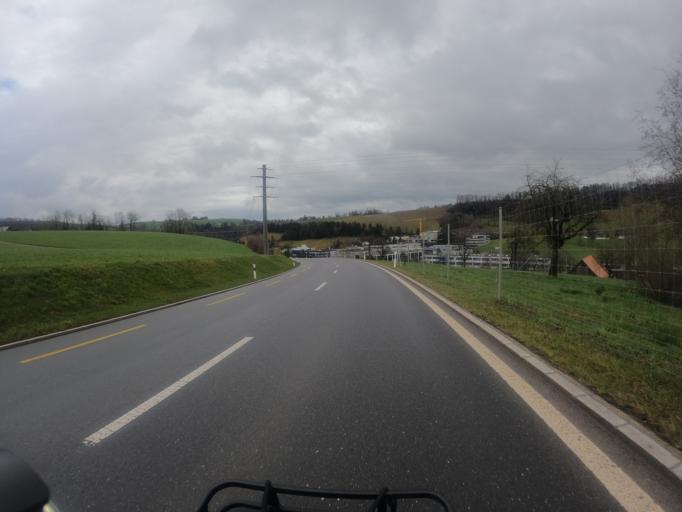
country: CH
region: Zug
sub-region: Zug
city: Baar
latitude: 47.2171
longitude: 8.5675
